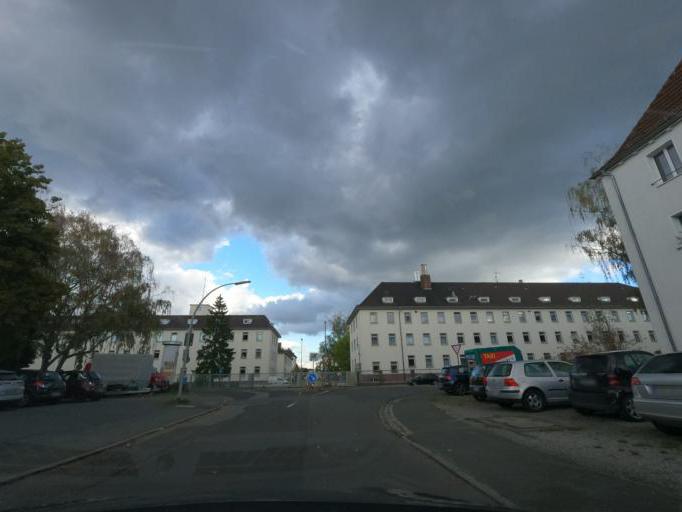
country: DE
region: Lower Saxony
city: Braunschweig
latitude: 52.2819
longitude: 10.5646
